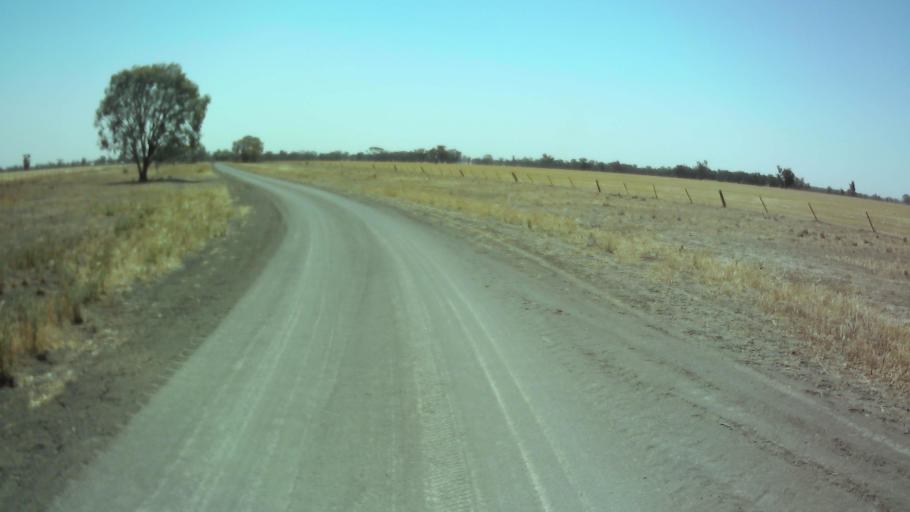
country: AU
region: New South Wales
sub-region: Weddin
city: Grenfell
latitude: -33.9922
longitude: 147.8642
